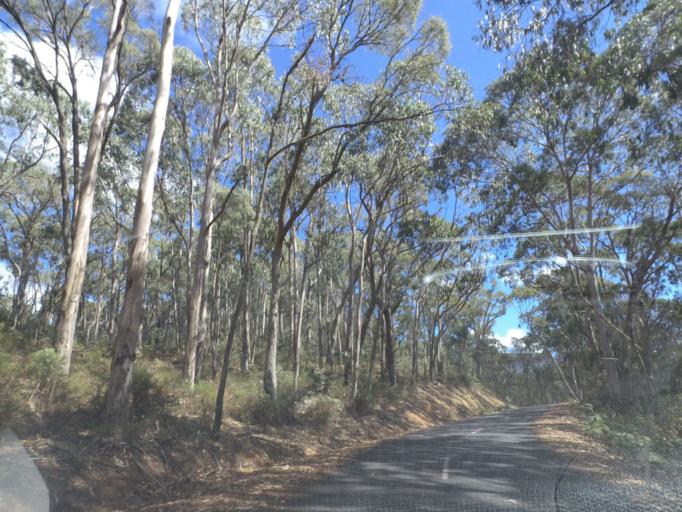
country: AU
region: Victoria
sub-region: Murrindindi
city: Alexandra
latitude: -37.3359
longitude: 145.9608
